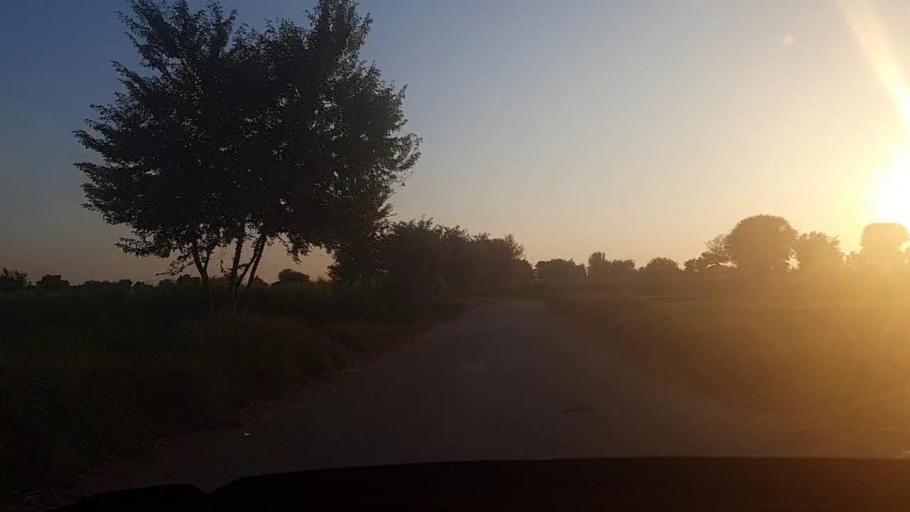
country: PK
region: Sindh
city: Sobhadero
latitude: 27.3491
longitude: 68.3760
